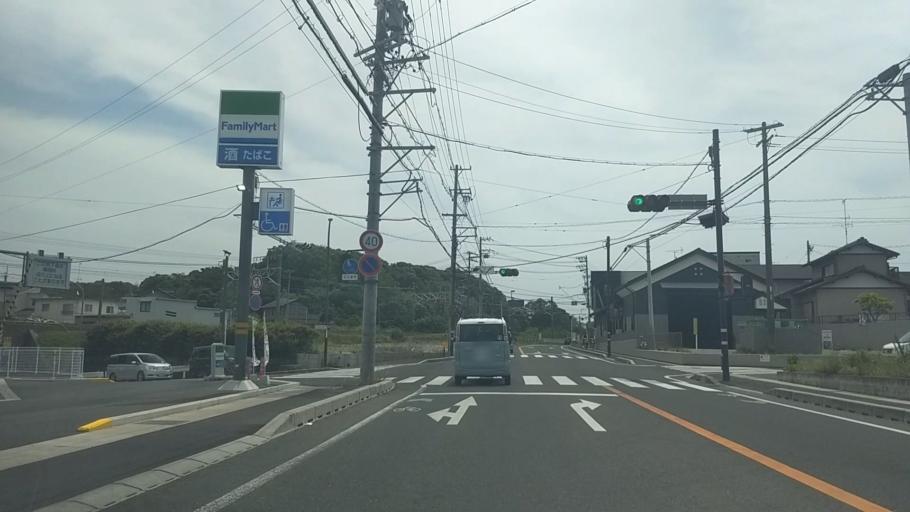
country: JP
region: Shizuoka
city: Kosai-shi
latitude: 34.7013
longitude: 137.5549
